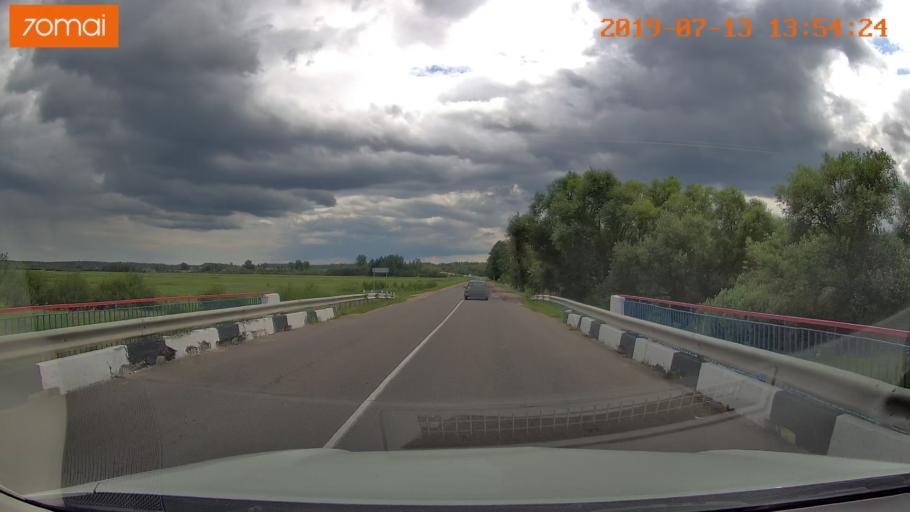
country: BY
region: Mogilev
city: Asipovichy
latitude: 53.2857
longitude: 28.6556
